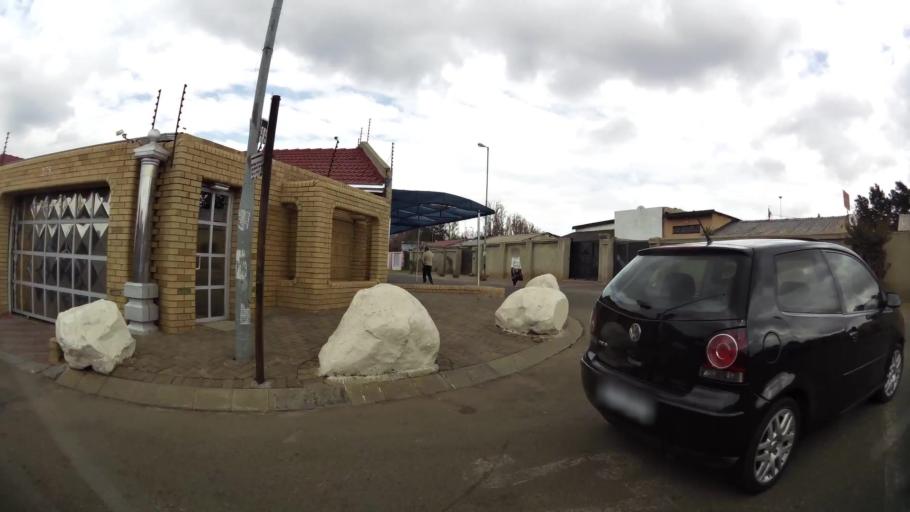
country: ZA
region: Gauteng
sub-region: City of Johannesburg Metropolitan Municipality
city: Soweto
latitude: -26.2697
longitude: 27.8727
